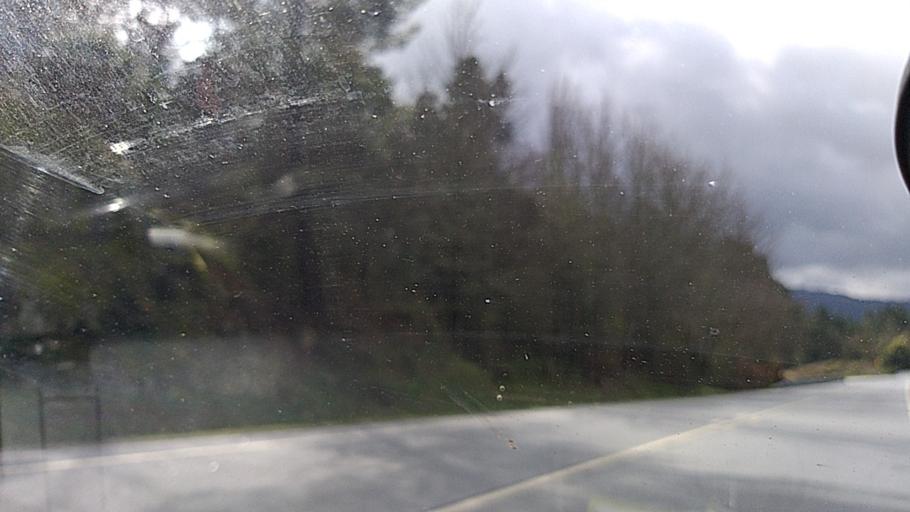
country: PT
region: Viseu
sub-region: Mangualde
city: Mangualde
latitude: 40.6503
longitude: -7.7330
